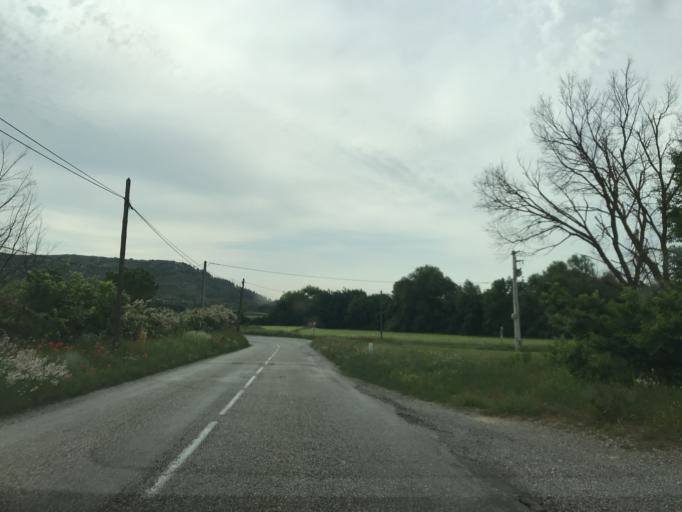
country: FR
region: Provence-Alpes-Cote d'Azur
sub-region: Departement du Vaucluse
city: Beaumont-de-Pertuis
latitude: 43.6777
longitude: 5.7274
